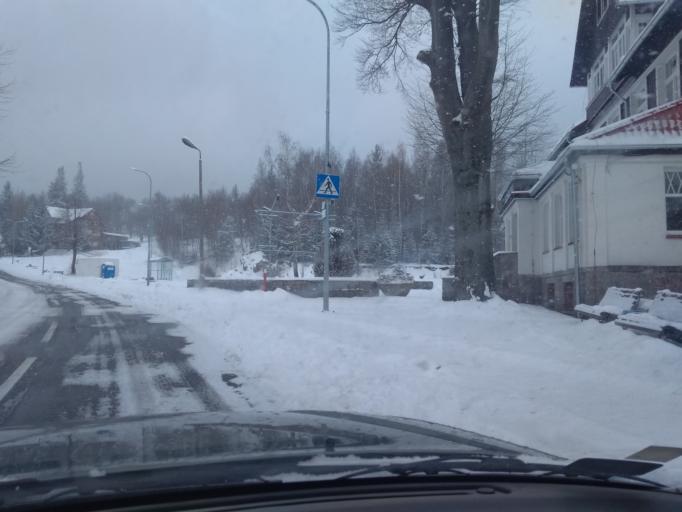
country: PL
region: Lower Silesian Voivodeship
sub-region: Powiat jeleniogorski
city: Sosnowka
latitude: 50.7861
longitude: 15.7214
